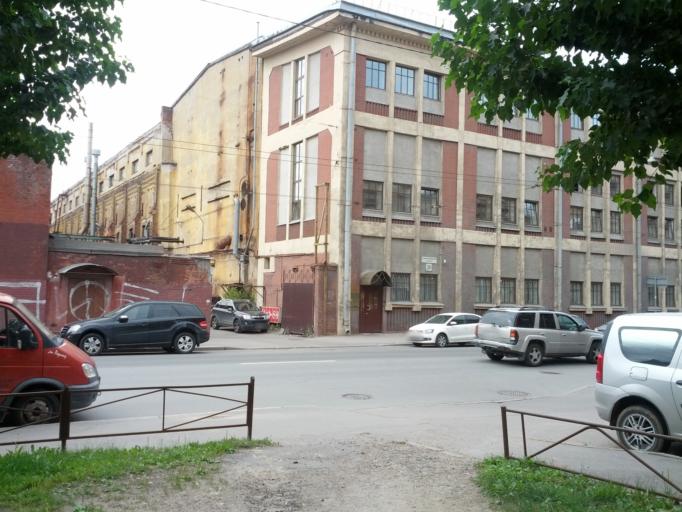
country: RU
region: Leningrad
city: Sampsonievskiy
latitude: 59.9656
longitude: 30.3435
